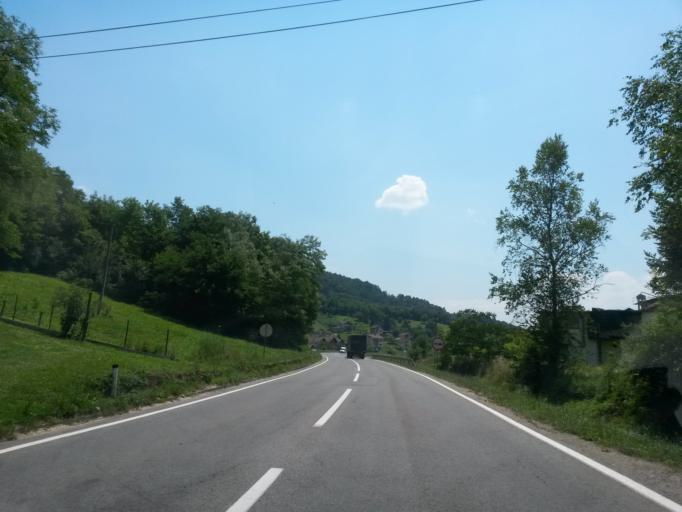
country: BA
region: Federation of Bosnia and Herzegovina
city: Lijesnica
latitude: 44.5110
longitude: 18.0812
